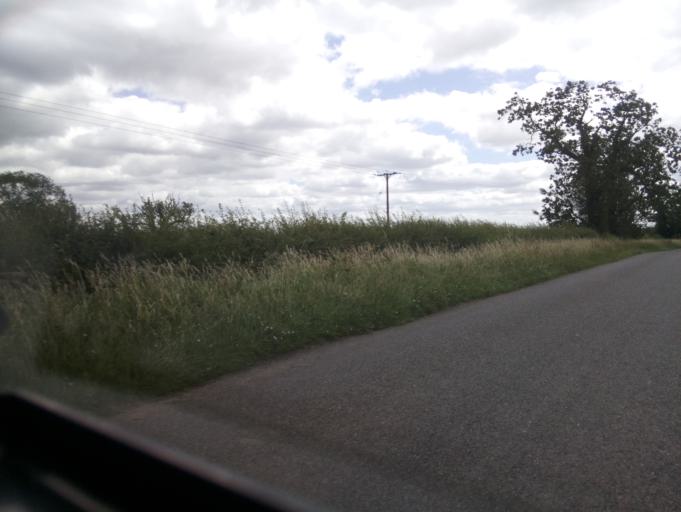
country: GB
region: England
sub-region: Nottinghamshire
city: Ruddington
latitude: 52.8495
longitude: -1.1048
